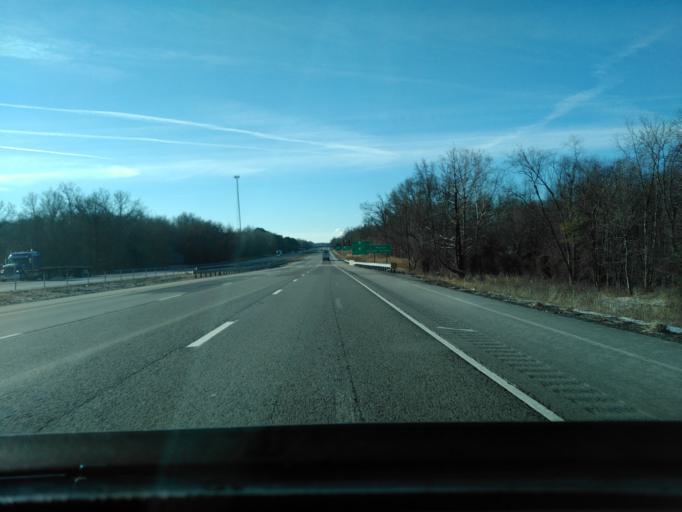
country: US
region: Illinois
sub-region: Williamson County
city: Johnston City
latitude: 37.8009
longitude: -88.9461
